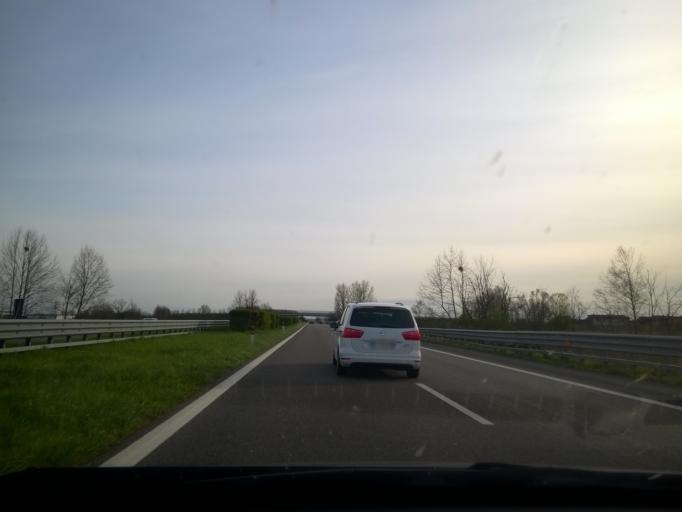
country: IT
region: Lombardy
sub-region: Provincia di Cremona
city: Corte de' Frati
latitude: 45.2176
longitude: 10.1109
